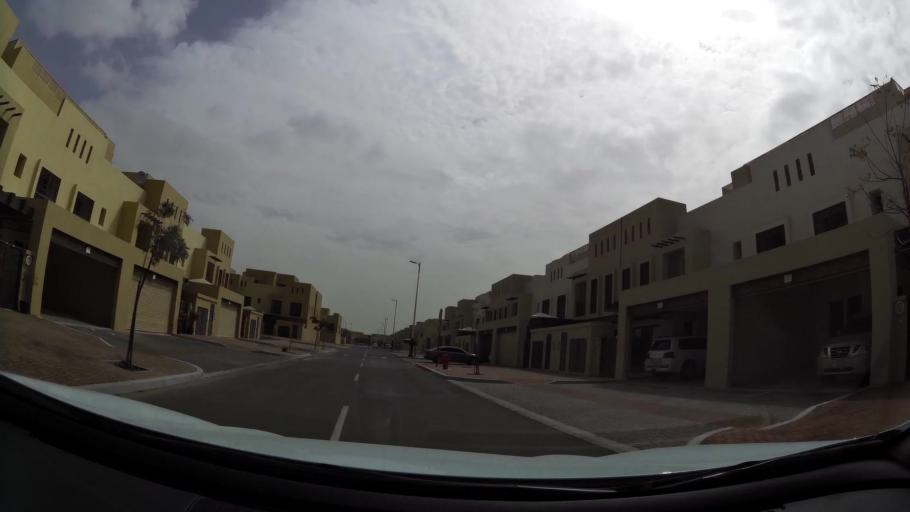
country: AE
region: Abu Dhabi
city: Abu Dhabi
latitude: 24.3985
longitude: 54.4890
